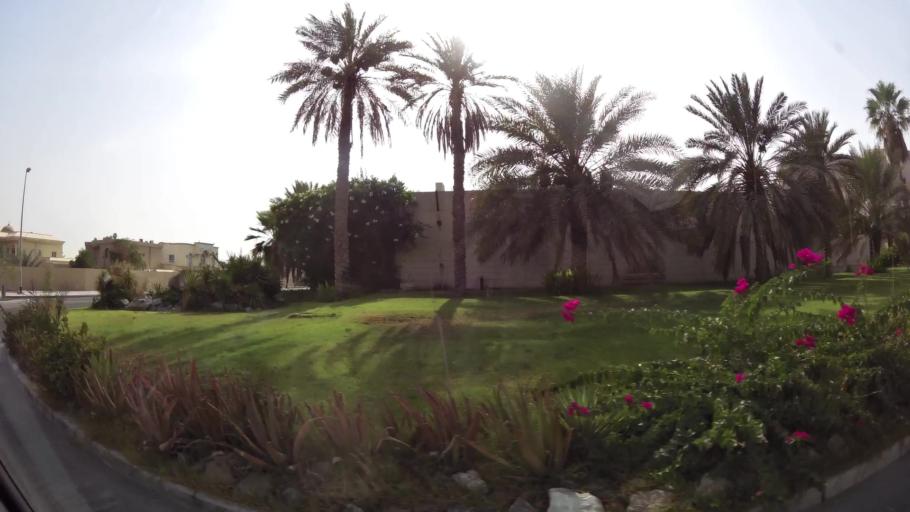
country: AE
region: Ash Shariqah
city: Sharjah
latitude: 25.2350
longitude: 55.4515
